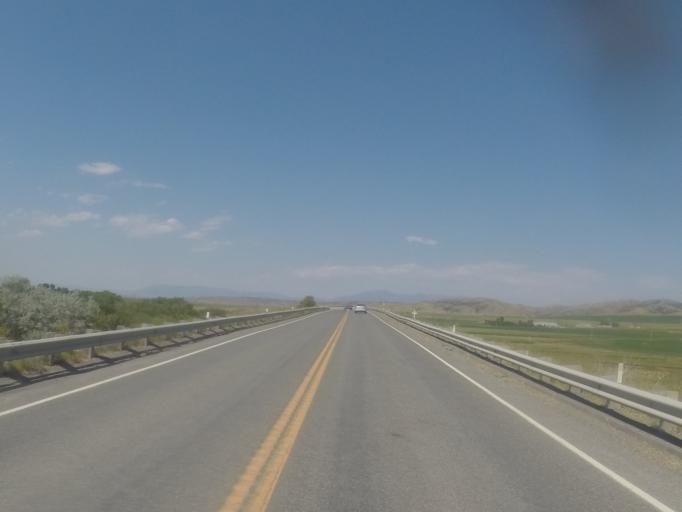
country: US
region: Montana
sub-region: Broadwater County
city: Townsend
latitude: 46.1753
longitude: -111.4448
